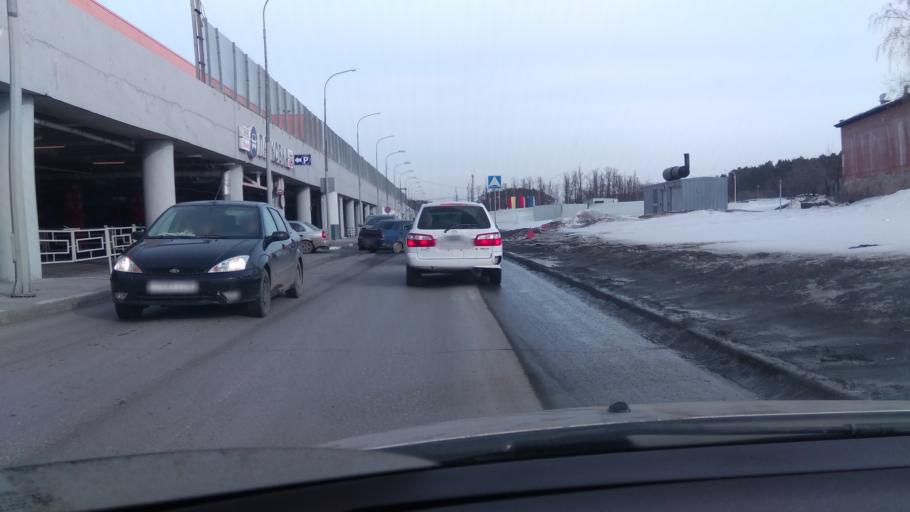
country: RU
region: Sverdlovsk
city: Shirokaya Rechka
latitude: 56.8220
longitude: 60.5036
